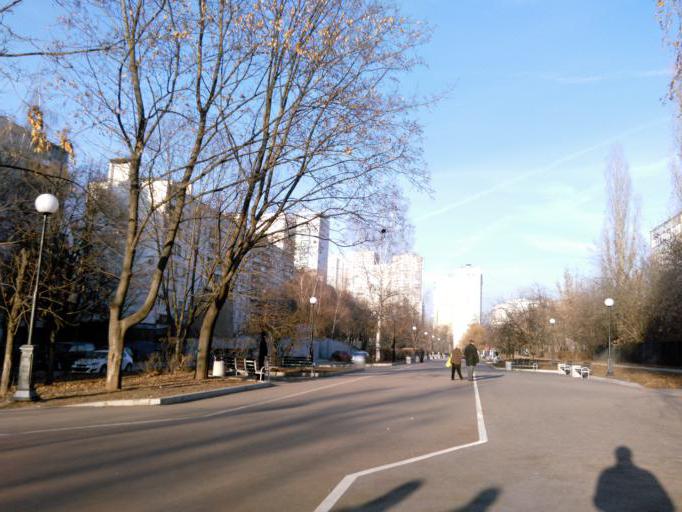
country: RU
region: Moscow
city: Troparevo
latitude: 55.6578
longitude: 37.4862
